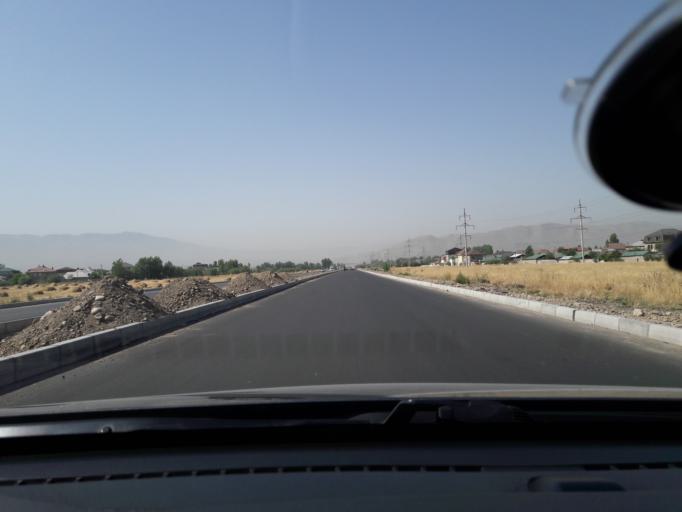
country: TJ
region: Dushanbe
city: Dushanbe
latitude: 38.4953
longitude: 68.7538
